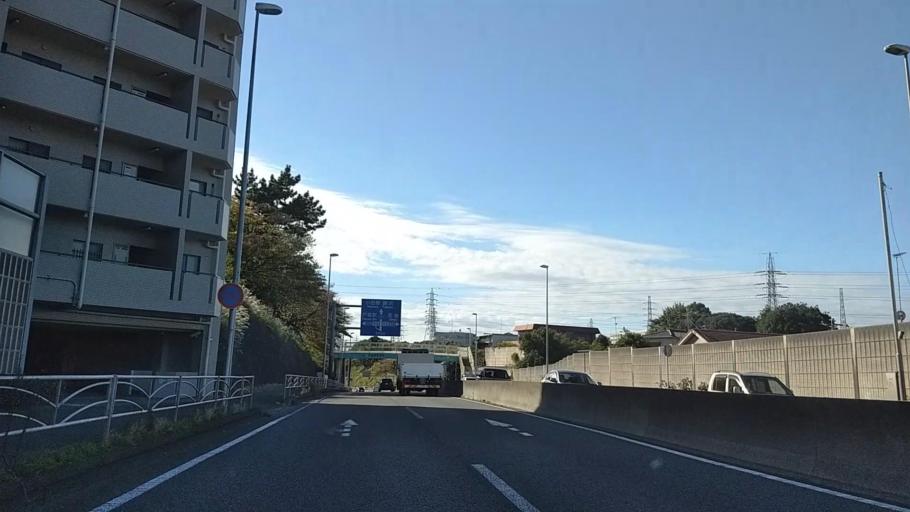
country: JP
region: Kanagawa
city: Fujisawa
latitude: 35.4051
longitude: 139.5281
